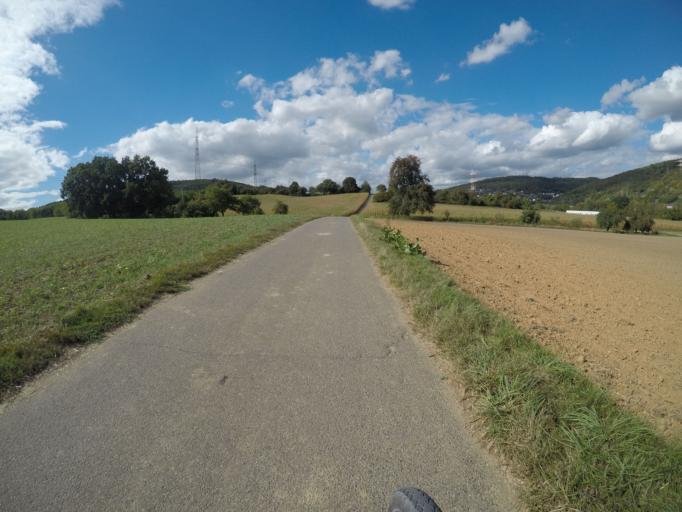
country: DE
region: Baden-Wuerttemberg
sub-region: Karlsruhe Region
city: Neckarzimmern
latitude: 49.3095
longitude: 9.1359
